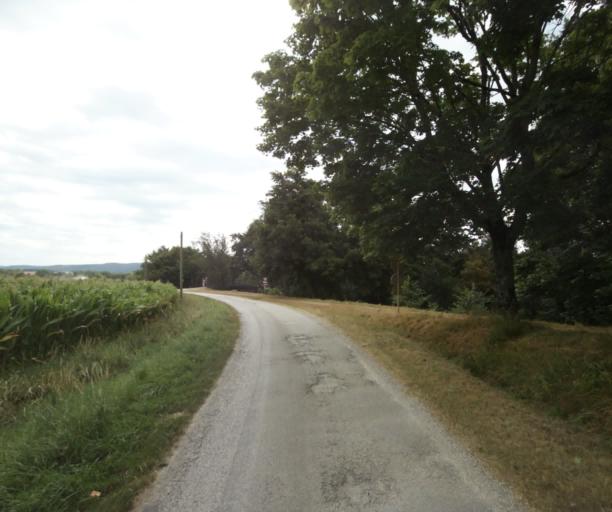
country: FR
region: Midi-Pyrenees
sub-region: Departement de la Haute-Garonne
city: Saint-Felix-Lauragais
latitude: 43.4307
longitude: 1.9444
